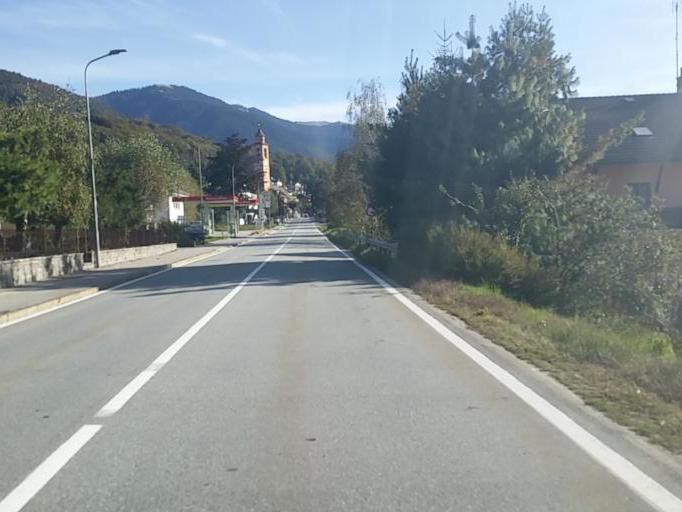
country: IT
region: Piedmont
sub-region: Provincia Verbano-Cusio-Ossola
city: Druogno
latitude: 46.1327
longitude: 8.4286
